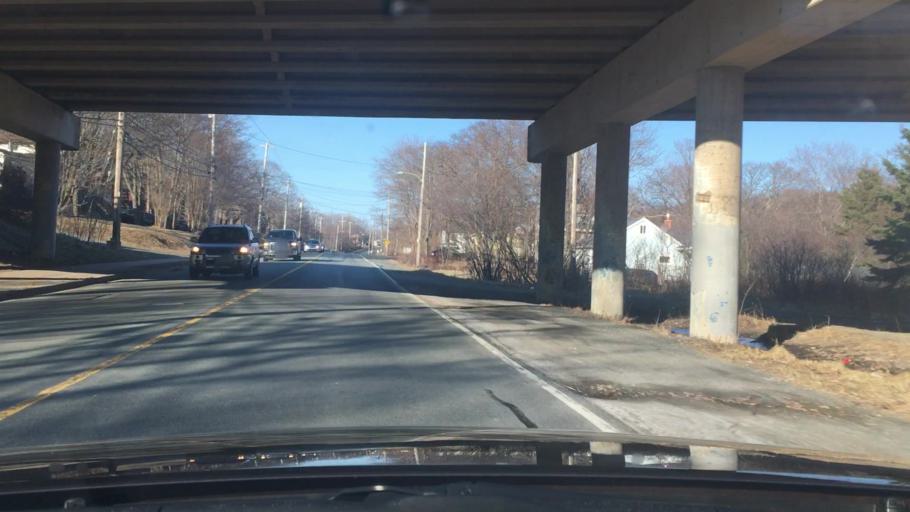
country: CA
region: Nova Scotia
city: Dartmouth
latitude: 44.7387
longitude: -63.6454
